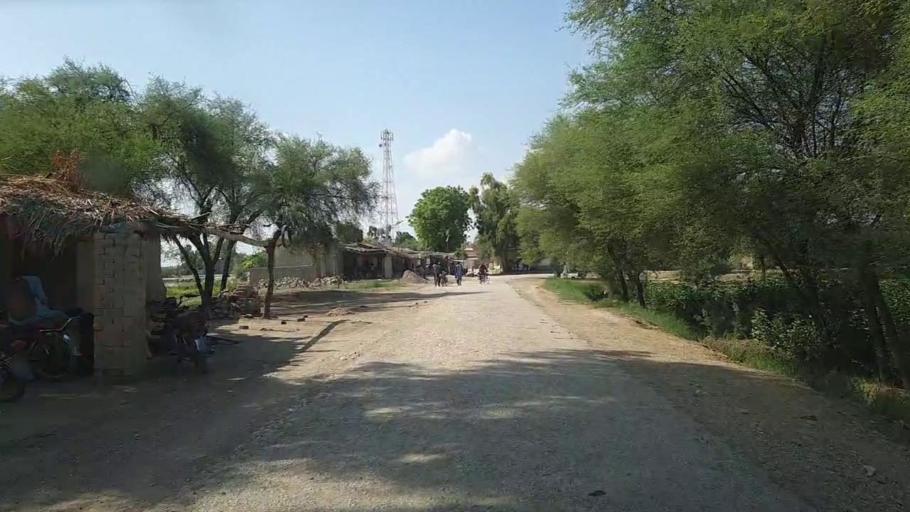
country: PK
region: Sindh
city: Khairpur
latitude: 28.1190
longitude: 69.6162
